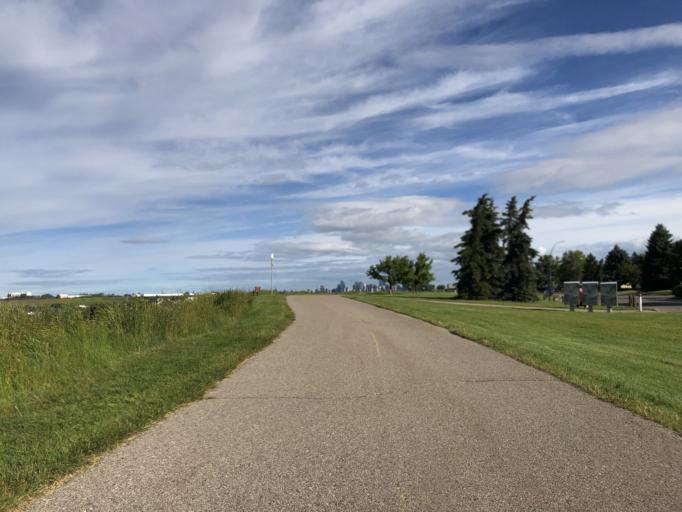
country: CA
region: Alberta
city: Calgary
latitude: 50.9909
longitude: -114.0201
